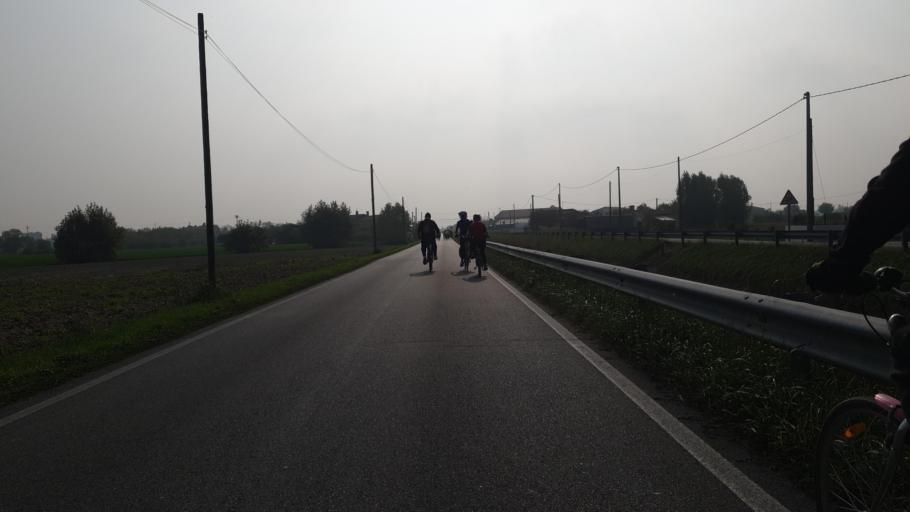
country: IT
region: Veneto
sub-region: Provincia di Padova
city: Corte
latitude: 45.3008
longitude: 12.0788
